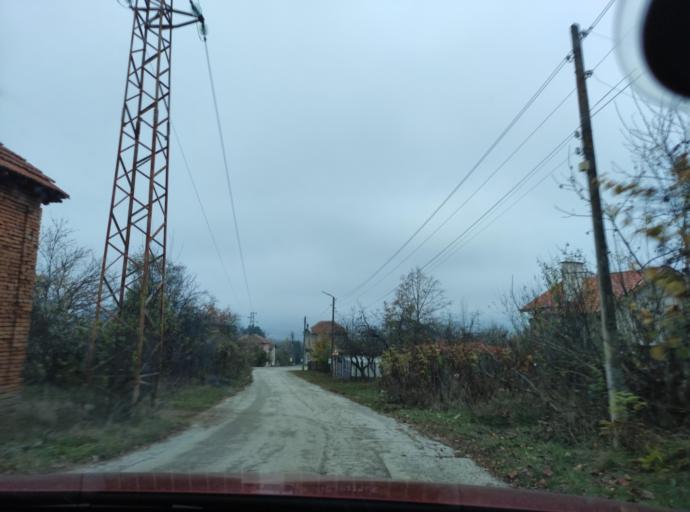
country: BG
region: Lovech
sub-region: Obshtina Yablanitsa
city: Yablanitsa
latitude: 43.0969
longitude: 24.0754
